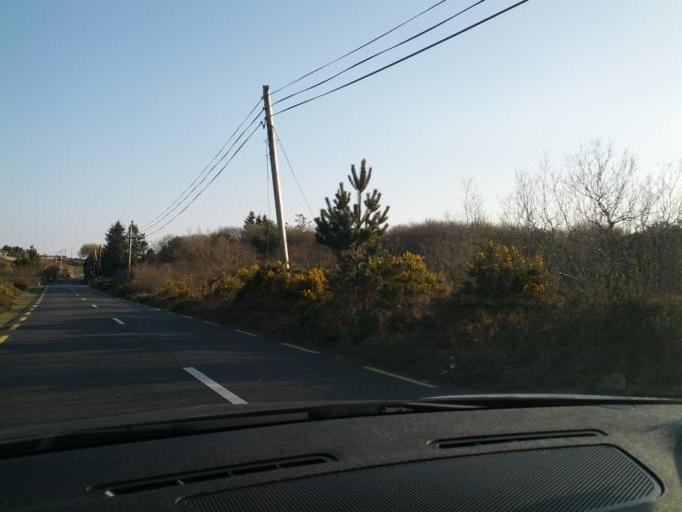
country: IE
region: Connaught
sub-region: County Galway
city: Oughterard
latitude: 53.3703
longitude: -9.5434
